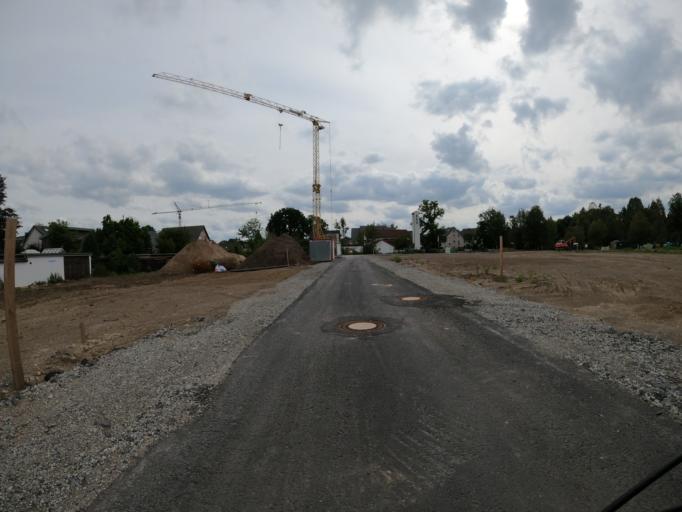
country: DE
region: North Rhine-Westphalia
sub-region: Regierungsbezirk Arnsberg
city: Lippstadt
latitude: 51.7132
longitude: 8.3387
